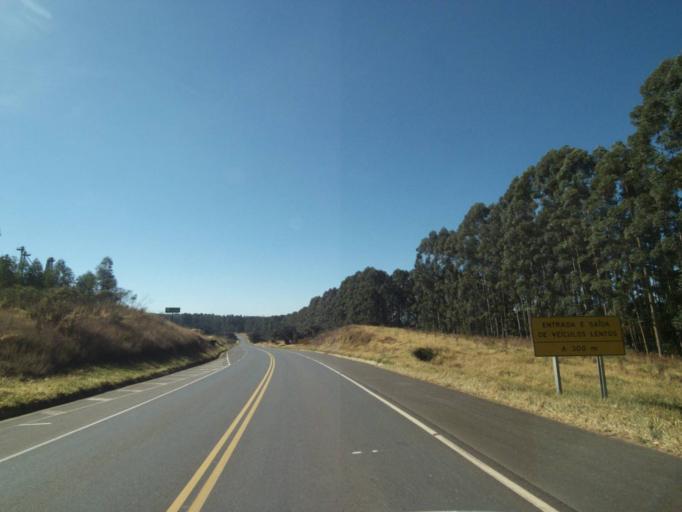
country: BR
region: Parana
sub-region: Tibagi
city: Tibagi
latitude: -24.5232
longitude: -50.4403
